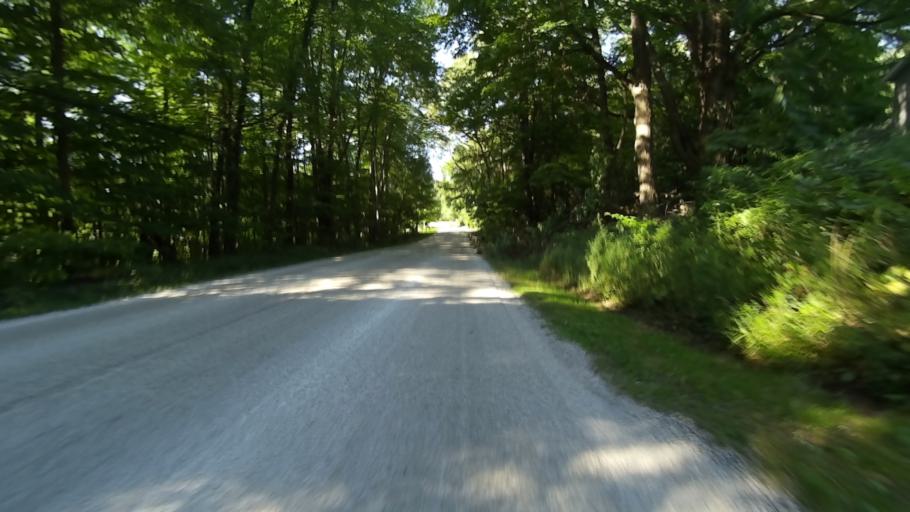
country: US
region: Ohio
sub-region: Portage County
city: Streetsboro
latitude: 41.2513
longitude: -81.2866
